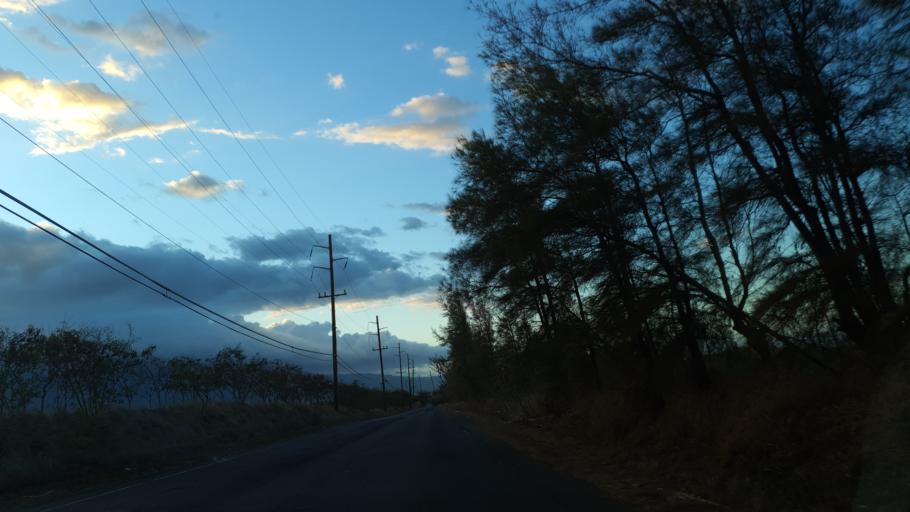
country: US
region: Hawaii
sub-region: Maui County
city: Kahului
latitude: 20.8683
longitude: -156.4351
